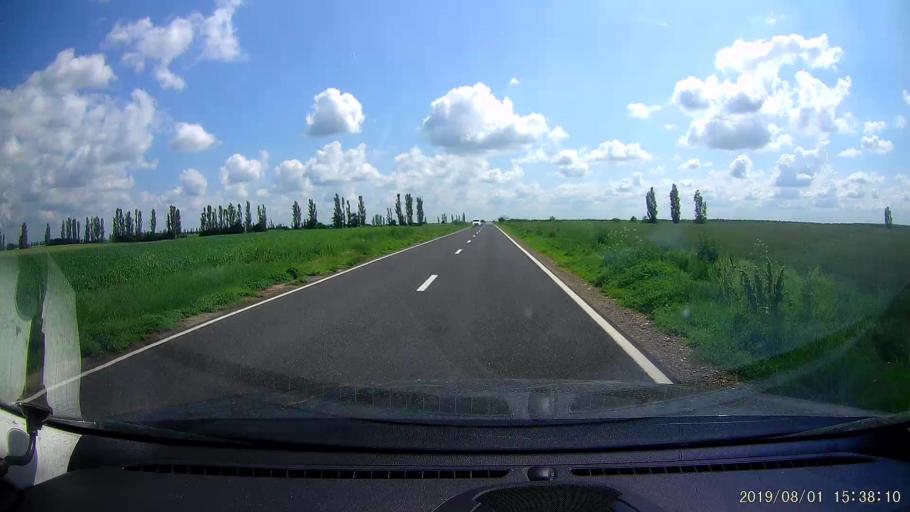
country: RO
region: Braila
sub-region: Comuna Insuratei
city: Insuratei
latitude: 44.8879
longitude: 27.5799
